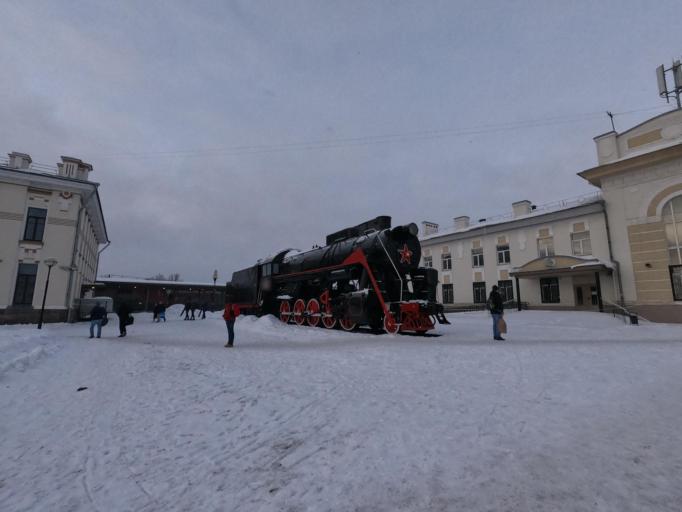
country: RU
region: Jaroslavl
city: Rybinsk
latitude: 58.0423
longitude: 38.8327
